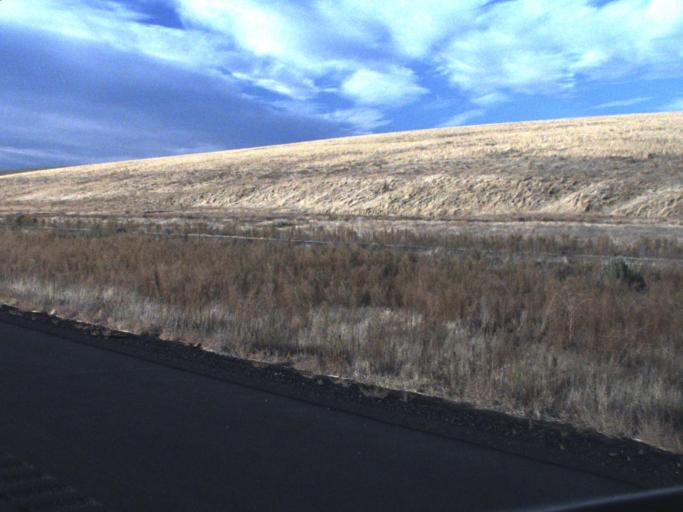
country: US
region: Washington
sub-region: Franklin County
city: Connell
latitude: 46.8665
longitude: -118.6321
